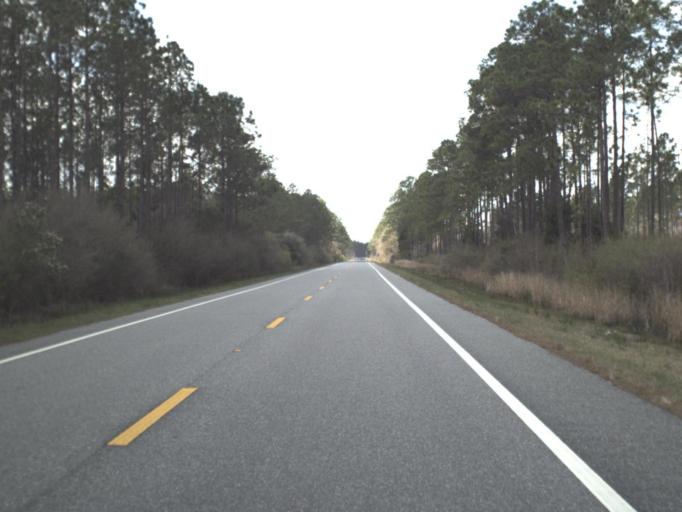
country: US
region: Florida
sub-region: Franklin County
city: Apalachicola
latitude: 29.8436
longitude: -84.9573
